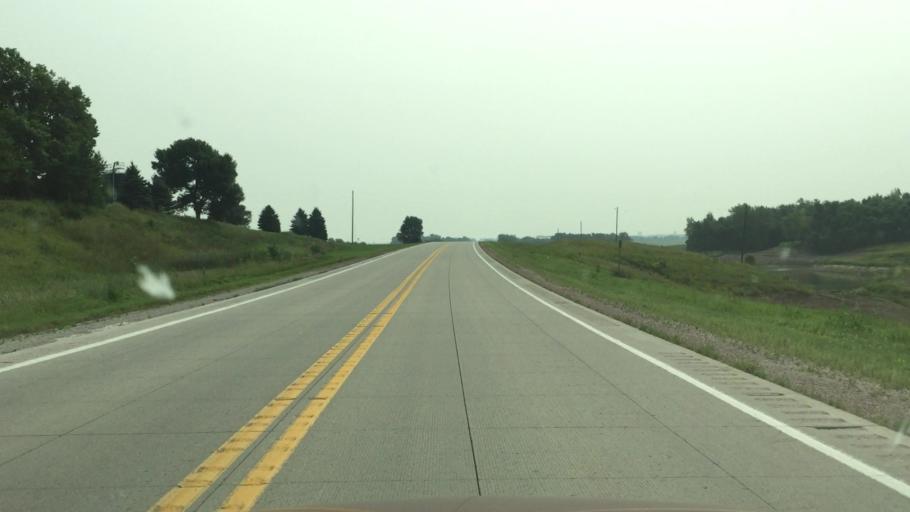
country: US
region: Iowa
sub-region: Osceola County
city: Sibley
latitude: 43.4330
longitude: -95.6203
